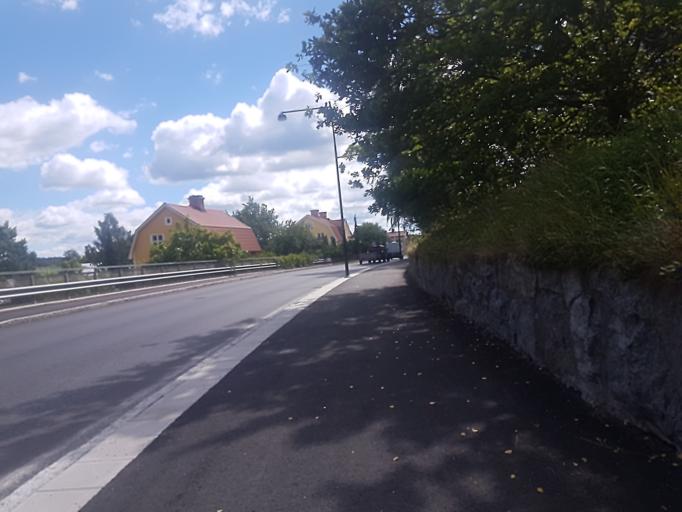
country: SE
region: Soedermanland
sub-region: Gnesta Kommun
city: Gnesta
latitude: 59.0442
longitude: 17.3242
